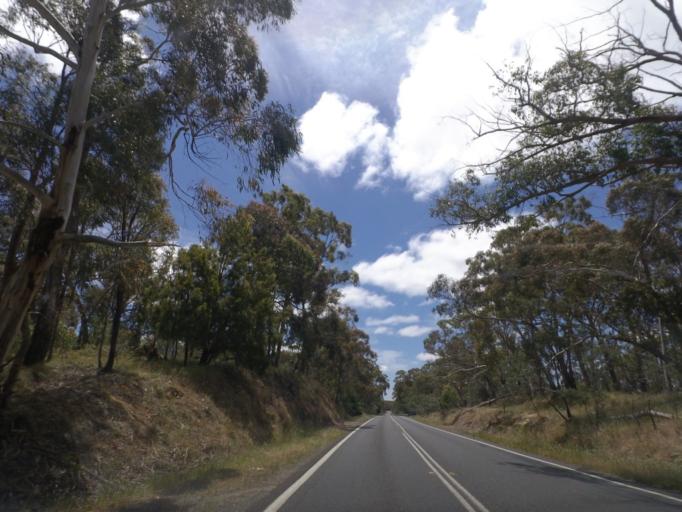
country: AU
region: Victoria
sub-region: Mount Alexander
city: Castlemaine
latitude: -37.2992
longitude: 144.1624
